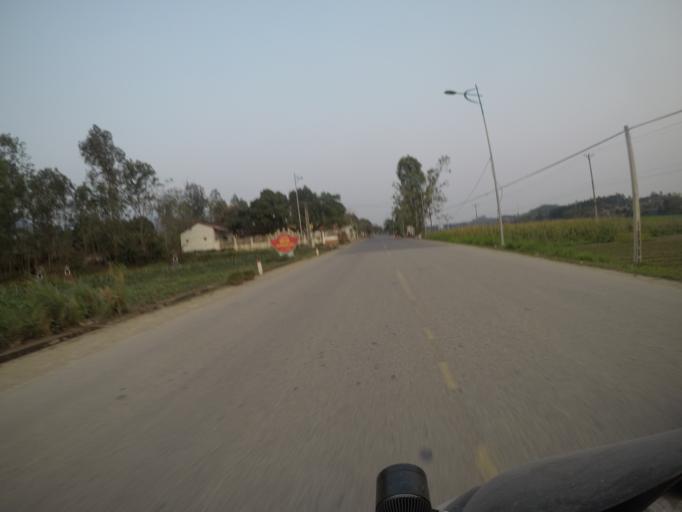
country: VN
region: Vinh Phuc
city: Trai Ngau
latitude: 21.4356
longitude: 105.5787
